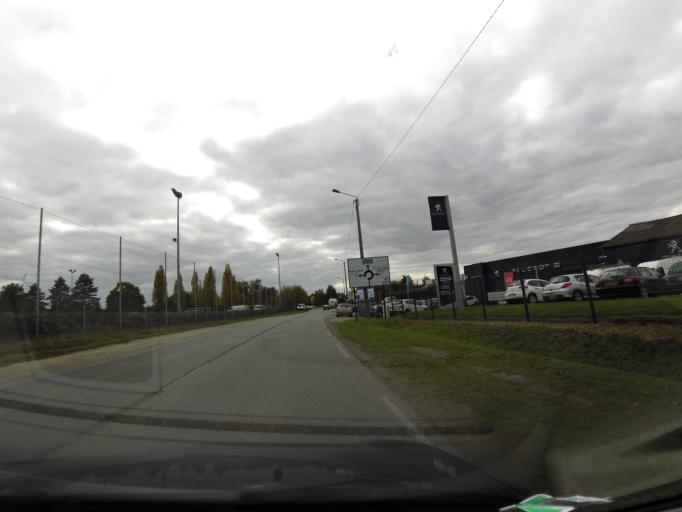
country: FR
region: Brittany
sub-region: Departement d'Ille-et-Vilaine
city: Vern-sur-Seiche
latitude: 48.0508
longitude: -1.6047
